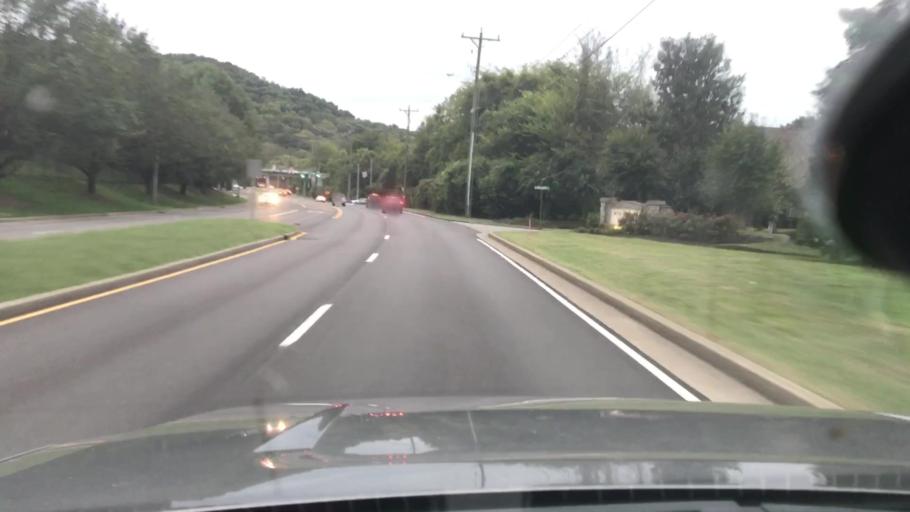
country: US
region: Tennessee
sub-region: Davidson County
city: Belle Meade
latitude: 36.0648
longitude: -86.9173
